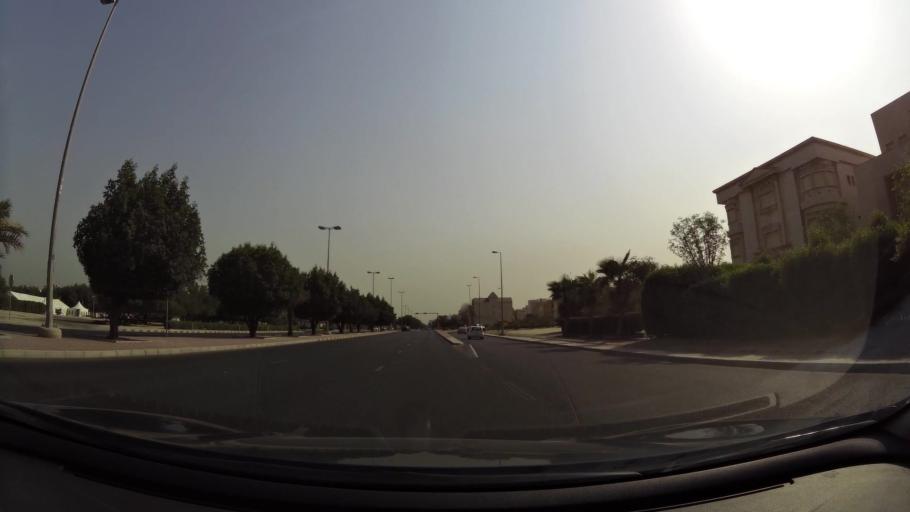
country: KW
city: Bayan
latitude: 29.2863
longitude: 48.0513
